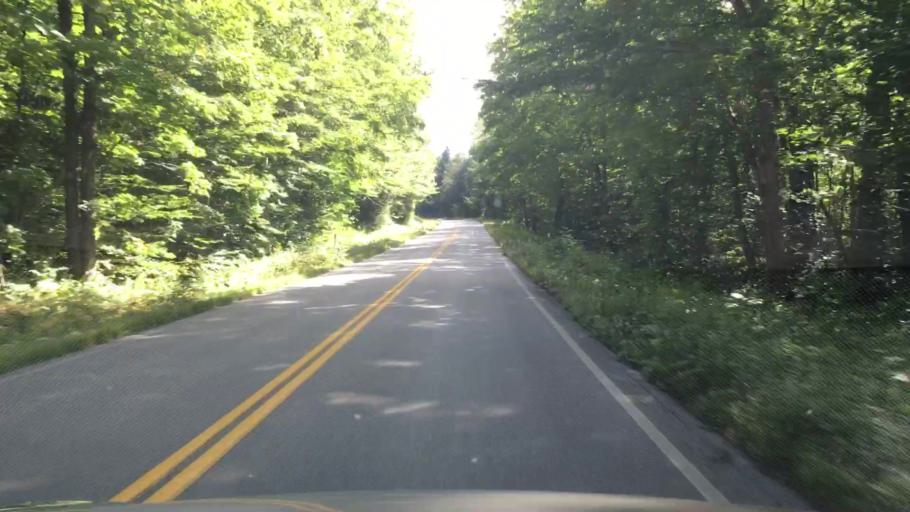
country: US
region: New Hampshire
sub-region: Carroll County
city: Tamworth
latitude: 44.0164
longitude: -71.3199
